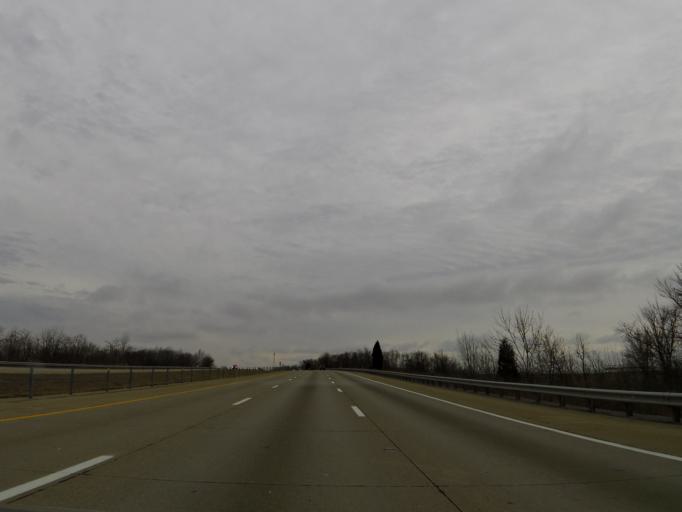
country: US
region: Kentucky
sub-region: Boone County
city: Hebron
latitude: 39.0766
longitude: -84.6863
